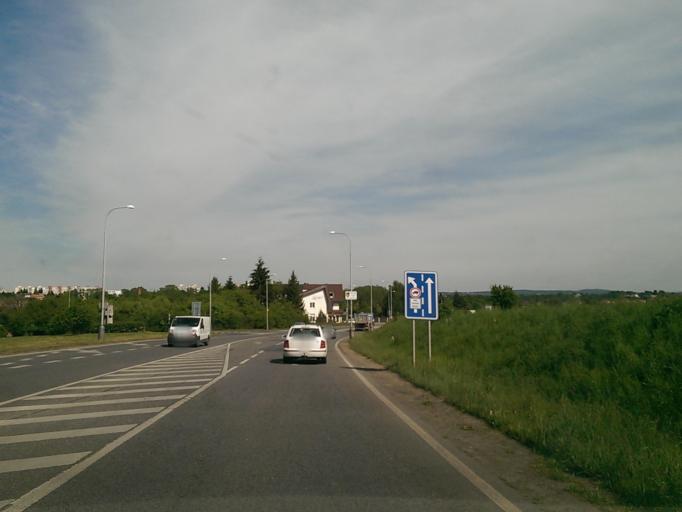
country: CZ
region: Central Bohemia
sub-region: Okres Praha-Zapad
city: Pruhonice
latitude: 50.0333
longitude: 14.5433
